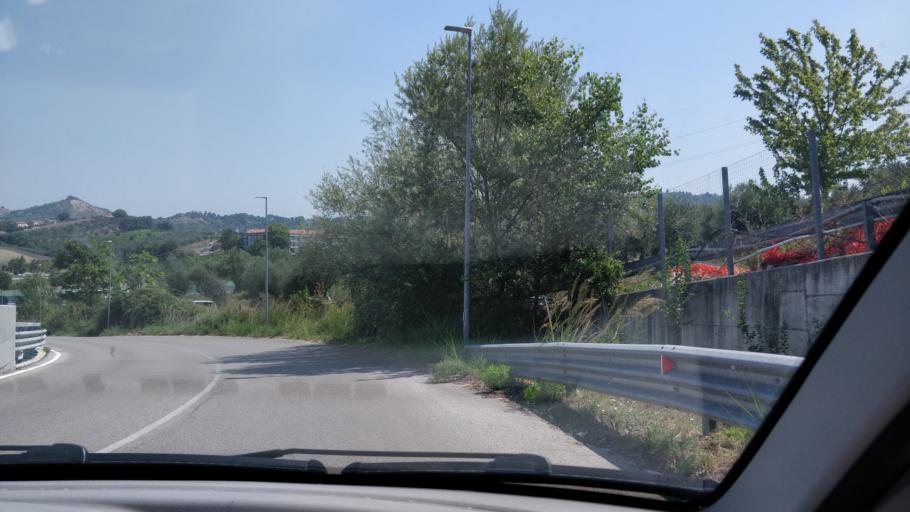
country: IT
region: Abruzzo
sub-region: Provincia di Chieti
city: Chieti
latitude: 42.3953
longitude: 14.1682
